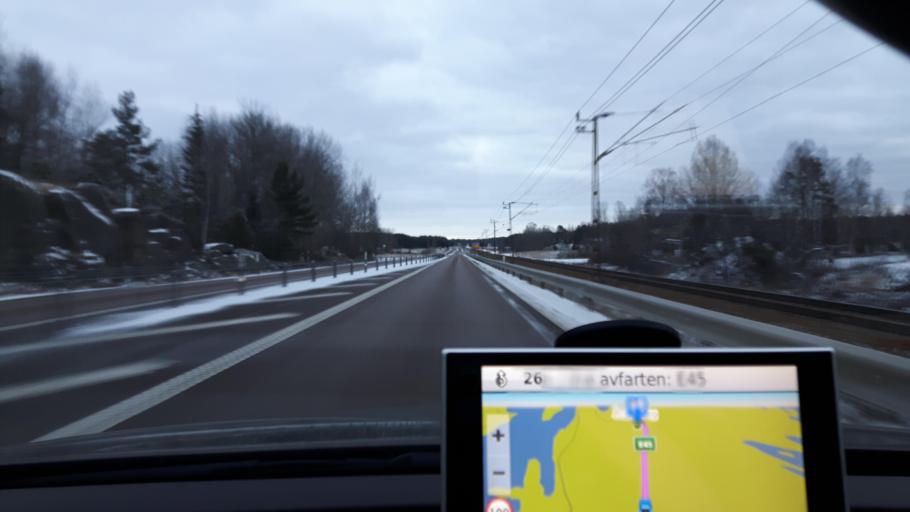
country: SE
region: Vaestra Goetaland
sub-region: Melleruds Kommun
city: Mellerud
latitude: 58.8494
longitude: 12.5522
